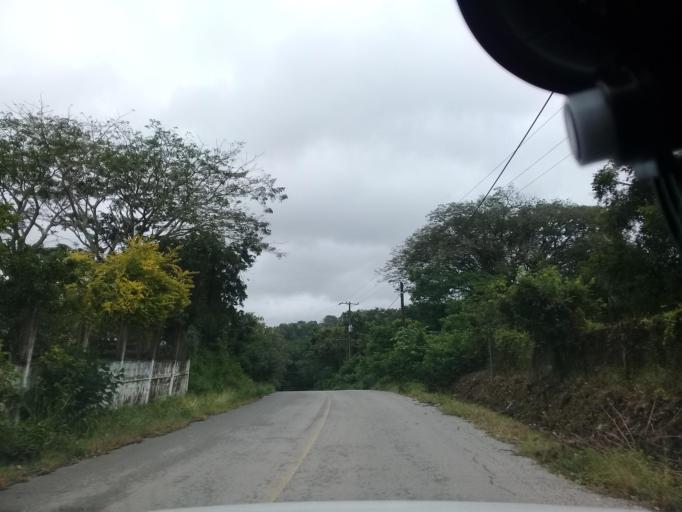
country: MX
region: Veracruz
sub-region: Chalma
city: San Pedro Coyutla
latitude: 21.2089
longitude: -98.4083
